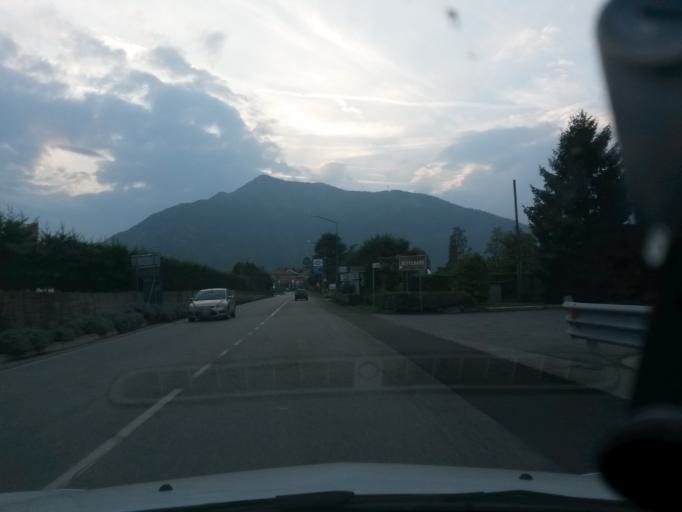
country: IT
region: Piedmont
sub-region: Provincia di Torino
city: Caselette
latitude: 45.1071
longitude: 7.5001
